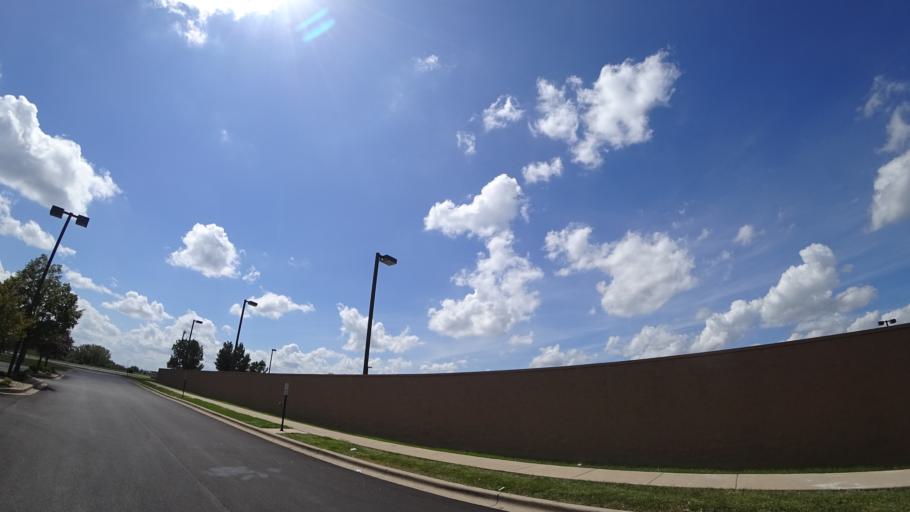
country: US
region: Illinois
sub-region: Cook County
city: Tinley Park
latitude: 41.5479
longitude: -87.7851
